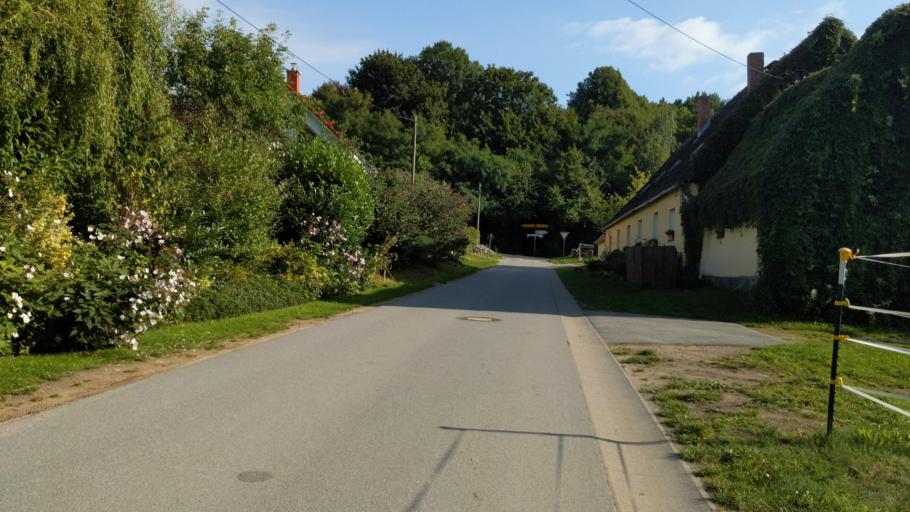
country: DE
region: Mecklenburg-Vorpommern
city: Kalkhorst
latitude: 54.0000
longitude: 11.0456
